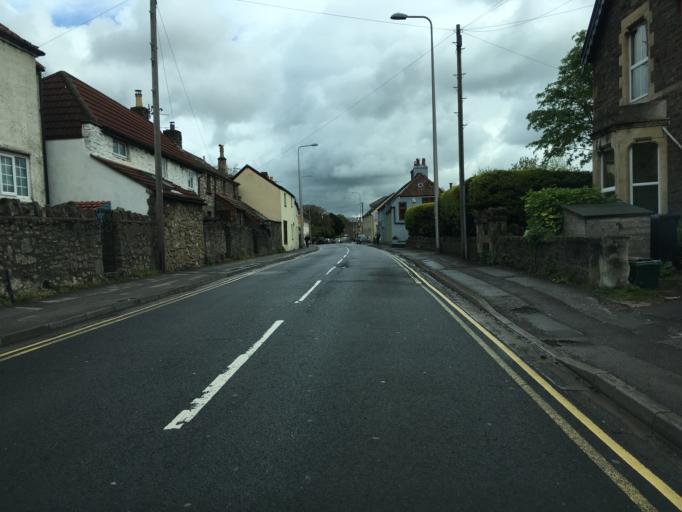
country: GB
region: England
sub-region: North Somerset
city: Clevedon
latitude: 51.4355
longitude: -2.8586
